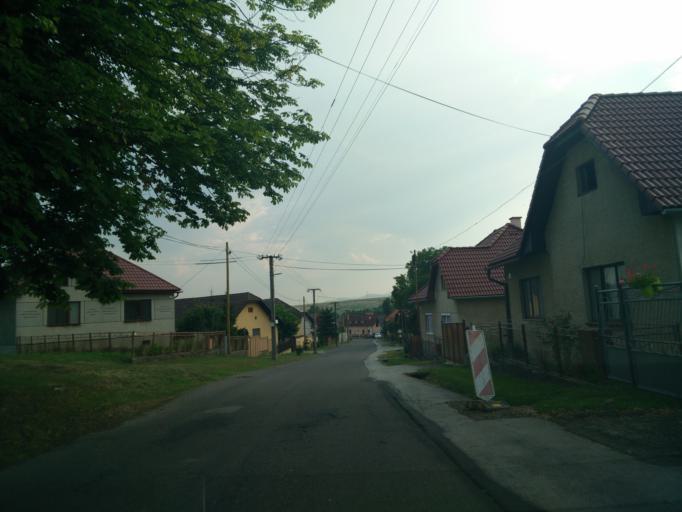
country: SK
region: Banskobystricky
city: Ziar nad Hronom
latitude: 48.6525
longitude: 18.8120
